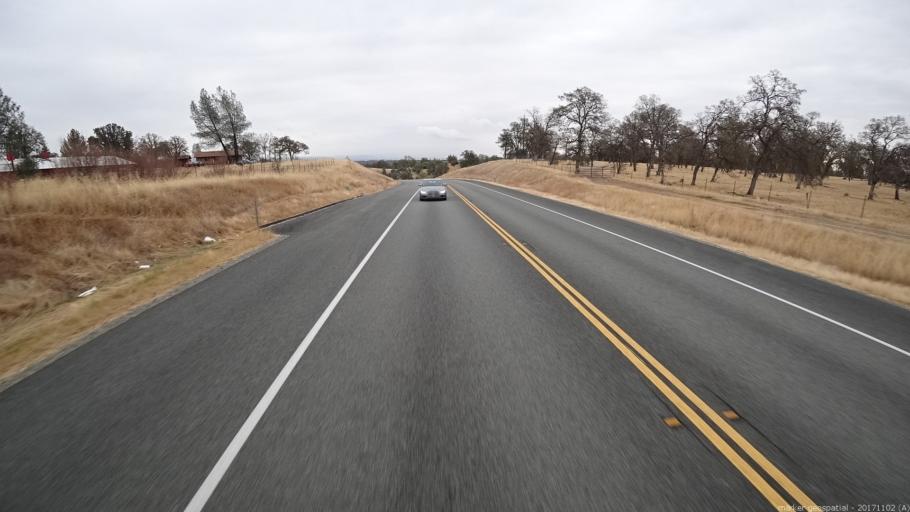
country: US
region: California
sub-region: Shasta County
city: Bella Vista
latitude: 40.6348
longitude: -122.2527
